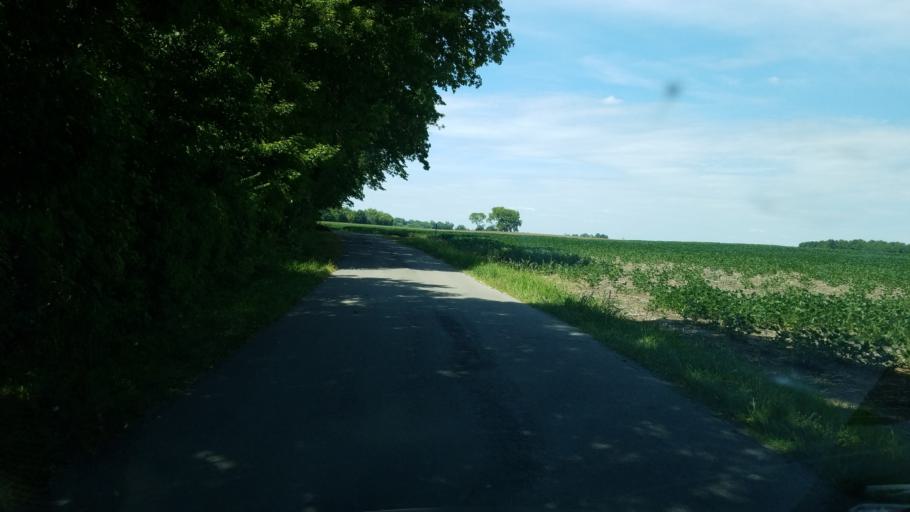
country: US
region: Ohio
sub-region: Marion County
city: Prospect
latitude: 40.3705
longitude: -83.1841
